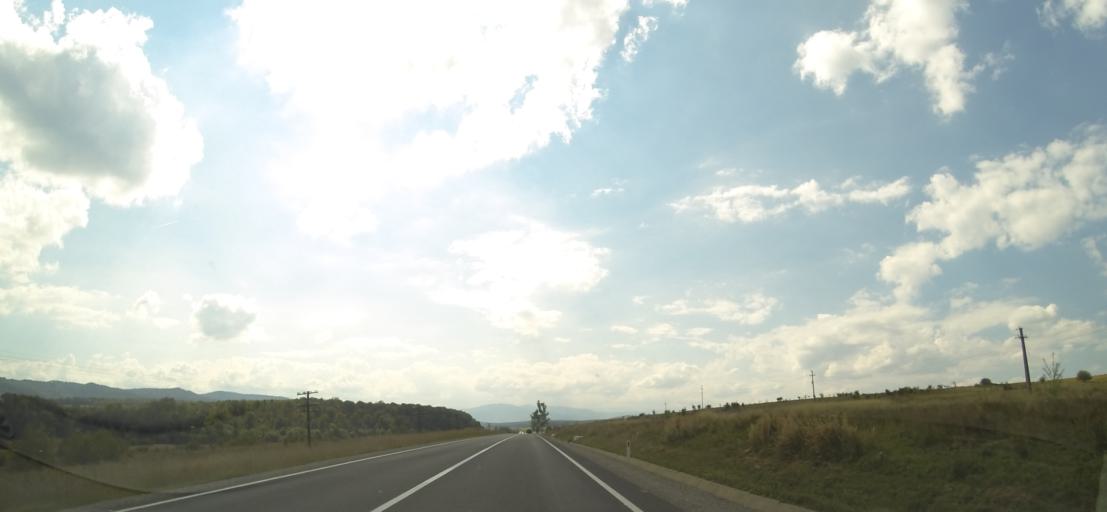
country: RO
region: Brasov
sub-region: Comuna Dumbravita
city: Dumbravita
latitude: 45.7641
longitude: 25.3269
